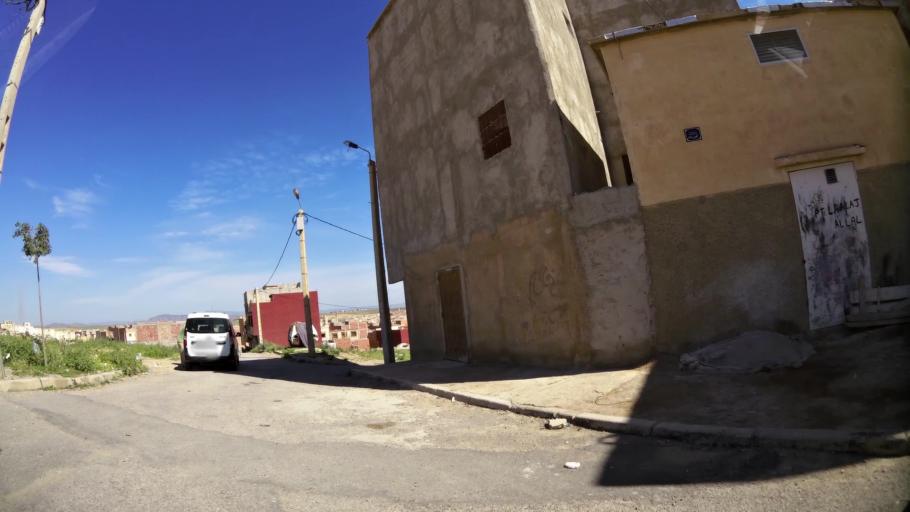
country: MA
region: Oriental
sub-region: Oujda-Angad
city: Oujda
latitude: 34.6549
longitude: -1.9371
